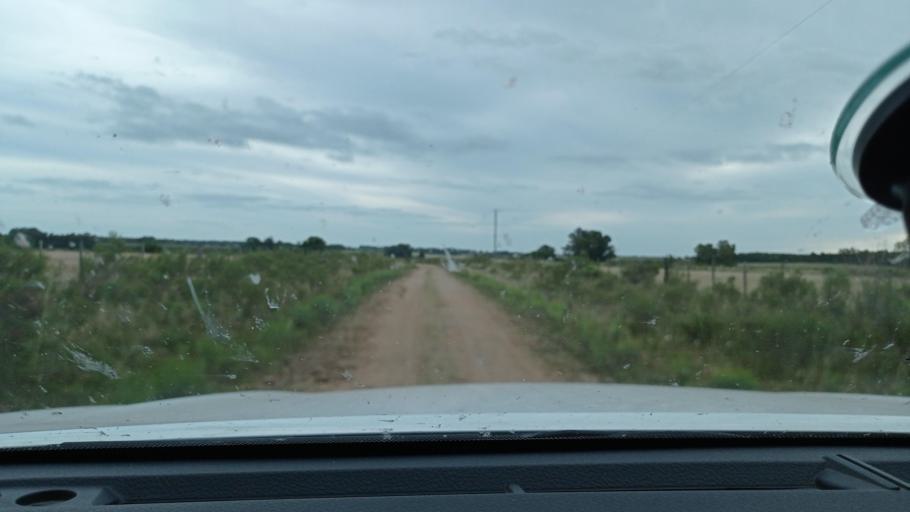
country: UY
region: Florida
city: Casupa
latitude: -34.1389
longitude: -55.8026
